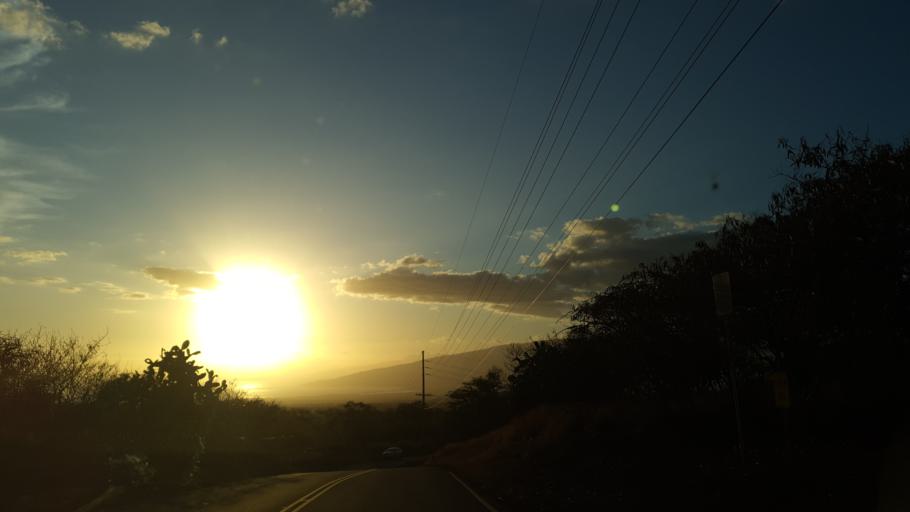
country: US
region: Hawaii
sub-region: Maui County
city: Pukalani
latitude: 20.7927
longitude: -156.3615
